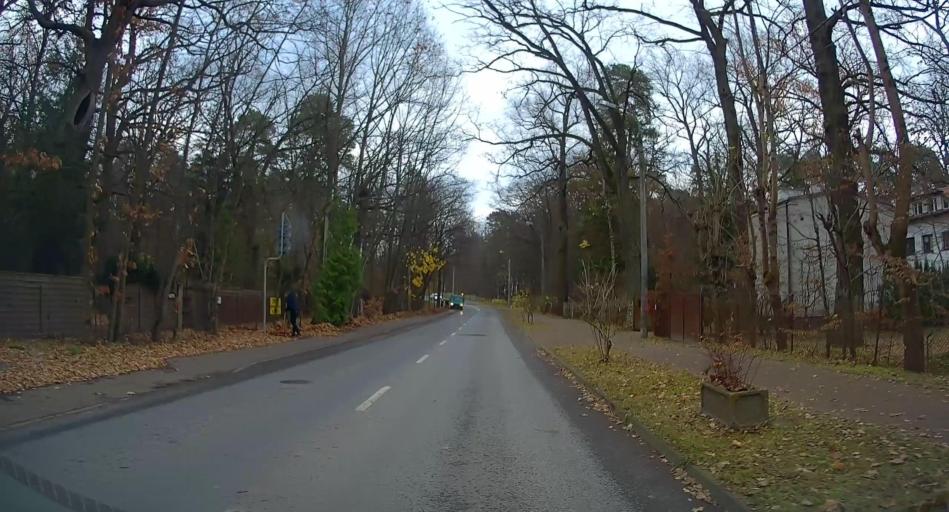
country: PL
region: Masovian Voivodeship
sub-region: Powiat piaseczynski
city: Piaseczno
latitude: 52.0600
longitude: 21.0195
